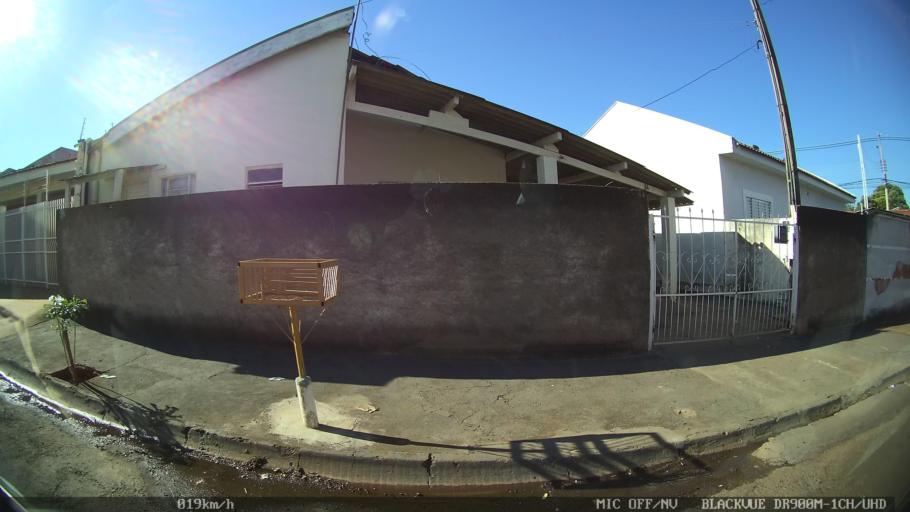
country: BR
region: Sao Paulo
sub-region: Olimpia
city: Olimpia
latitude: -20.7412
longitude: -48.8940
